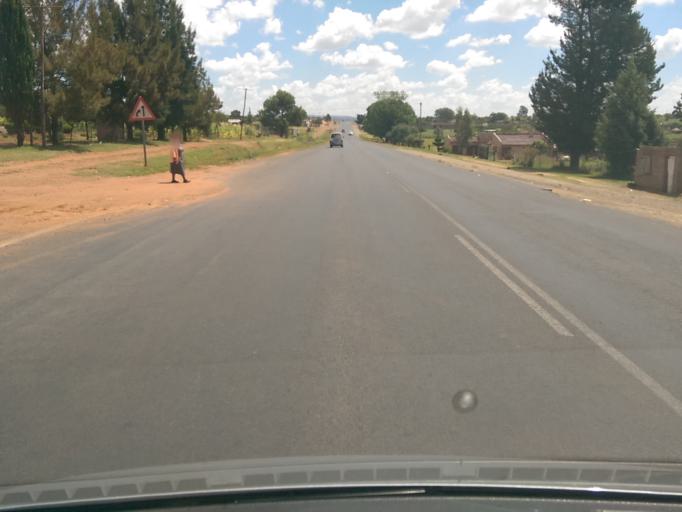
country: LS
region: Maseru
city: Maseru
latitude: -29.4086
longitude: 27.5897
